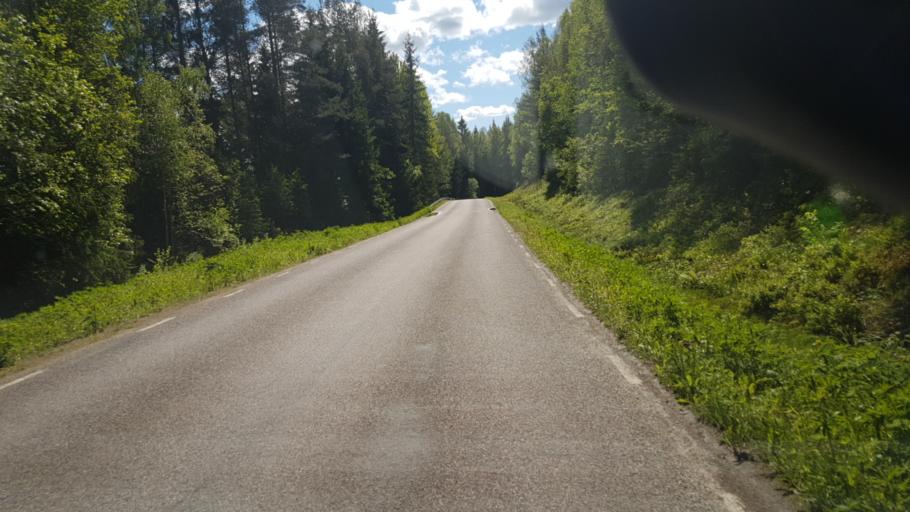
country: SE
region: Vaermland
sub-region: Grums Kommun
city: Grums
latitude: 59.5095
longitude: 12.8678
